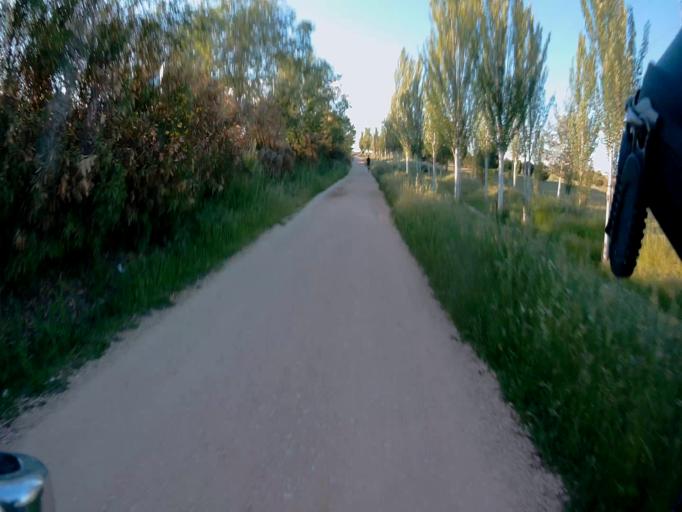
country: ES
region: Madrid
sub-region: Provincia de Madrid
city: Fuenlabrada
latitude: 40.3087
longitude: -3.7982
